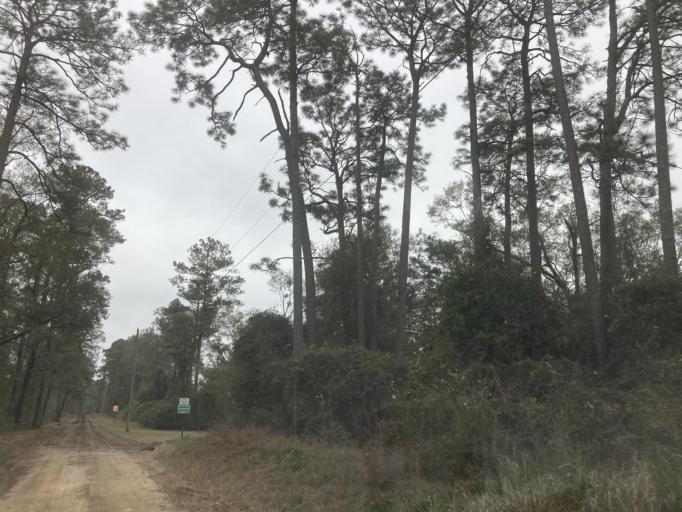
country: US
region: Mississippi
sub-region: Jackson County
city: Latimer
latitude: 30.6779
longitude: -88.9134
